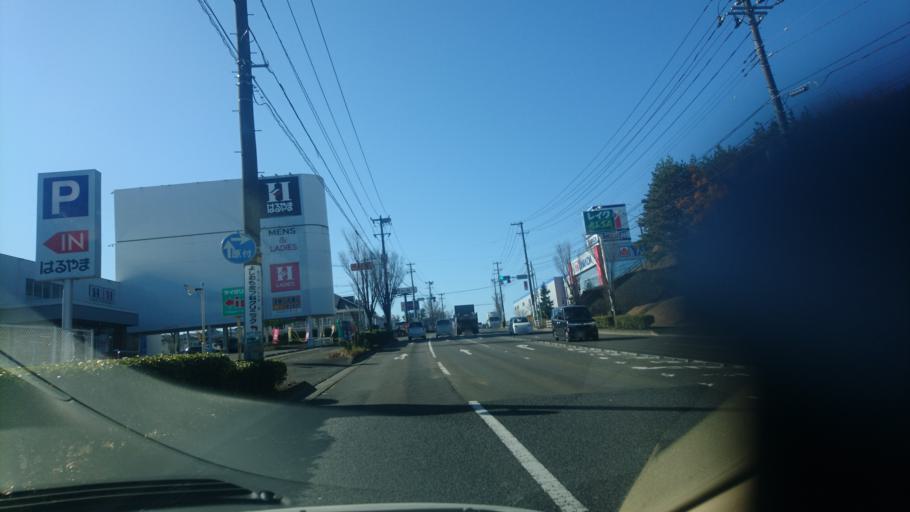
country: JP
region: Miyagi
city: Sendai-shi
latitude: 38.2958
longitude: 140.8265
